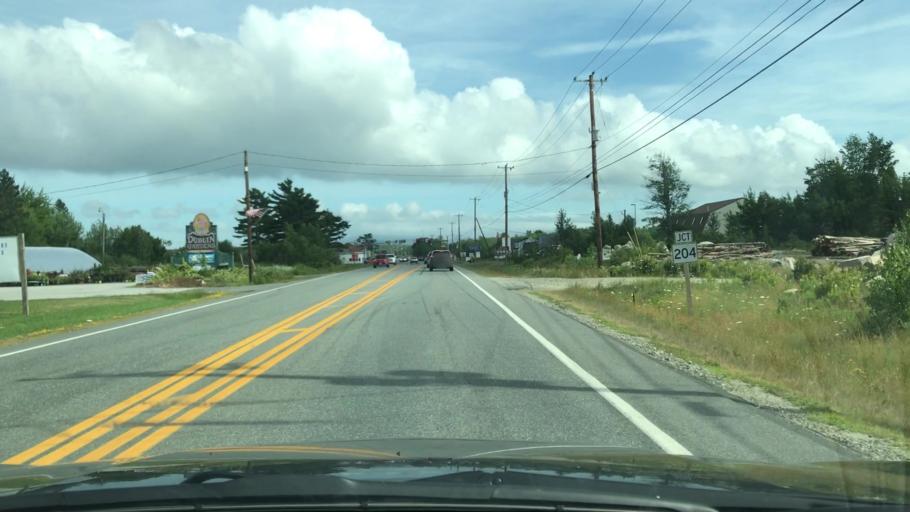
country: US
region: Maine
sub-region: Hancock County
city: Trenton
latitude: 44.4903
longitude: -68.3727
